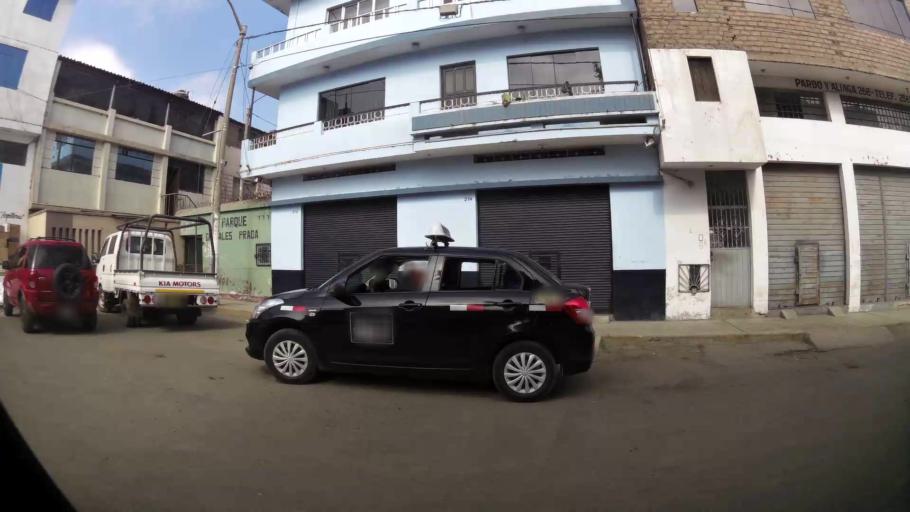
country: PE
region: La Libertad
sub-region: Provincia de Trujillo
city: Trujillo
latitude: -8.1124
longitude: -79.0166
